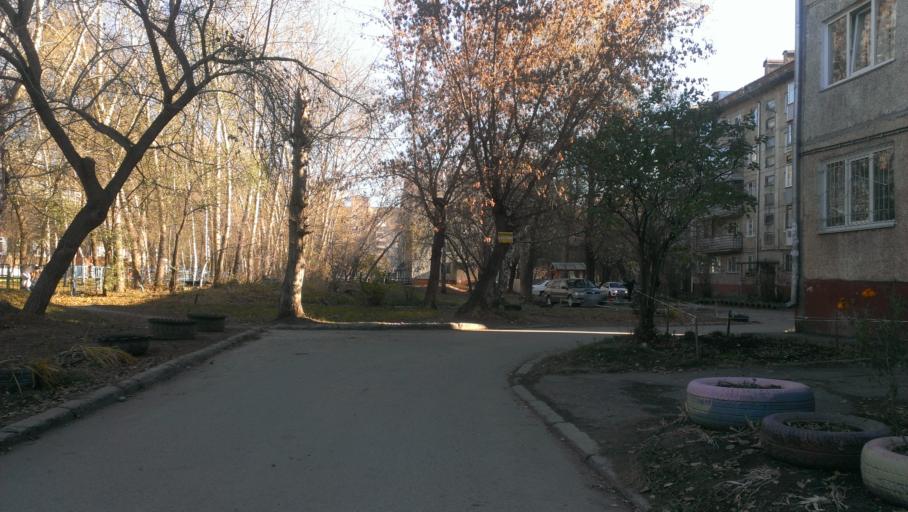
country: RU
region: Altai Krai
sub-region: Gorod Barnaulskiy
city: Barnaul
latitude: 53.3447
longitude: 83.6904
